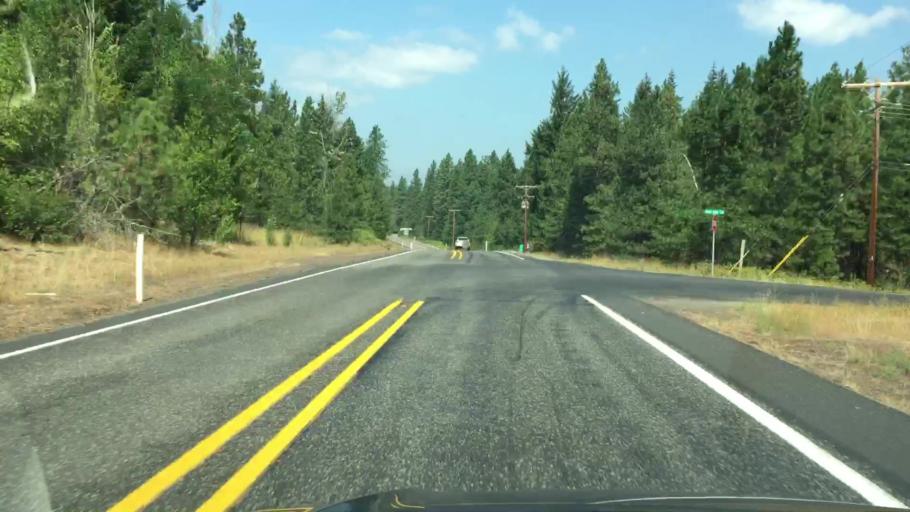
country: US
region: Washington
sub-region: Klickitat County
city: White Salmon
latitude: 45.9637
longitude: -121.4902
